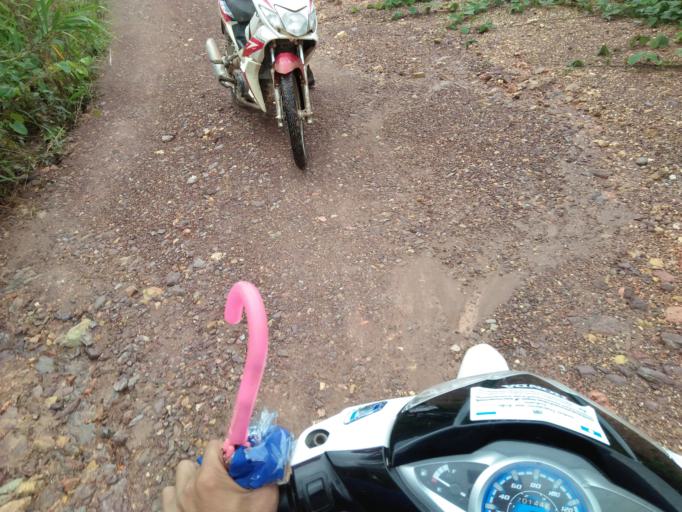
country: TH
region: Nan
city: Chaloem Phra Kiat
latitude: 19.7594
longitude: 100.7441
